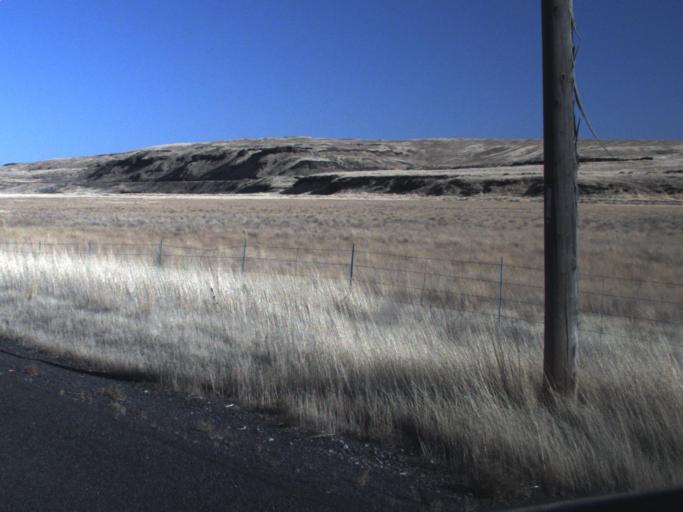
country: US
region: Washington
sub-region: Adams County
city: Ritzville
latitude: 46.7366
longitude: -118.3431
